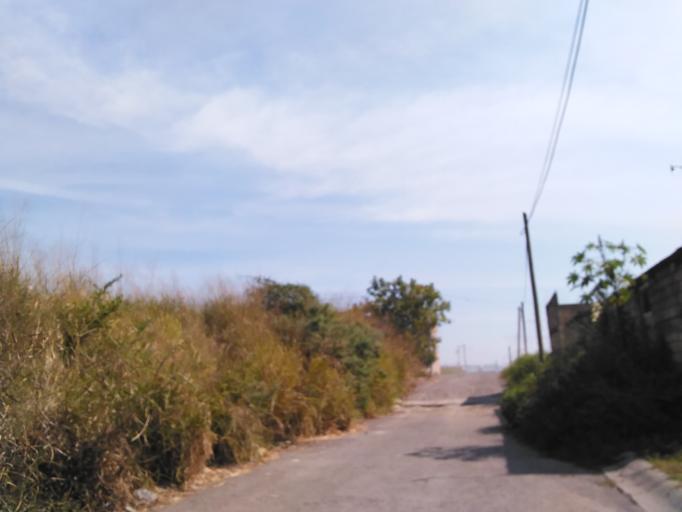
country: MX
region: Nayarit
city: Tepic
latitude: 21.4915
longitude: -104.8524
